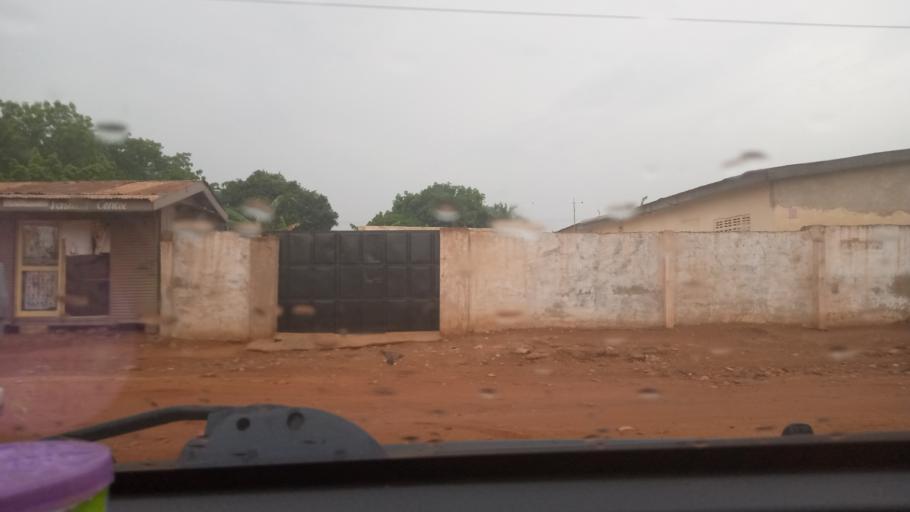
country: GH
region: Greater Accra
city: Medina Estates
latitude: 5.7029
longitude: -0.1671
